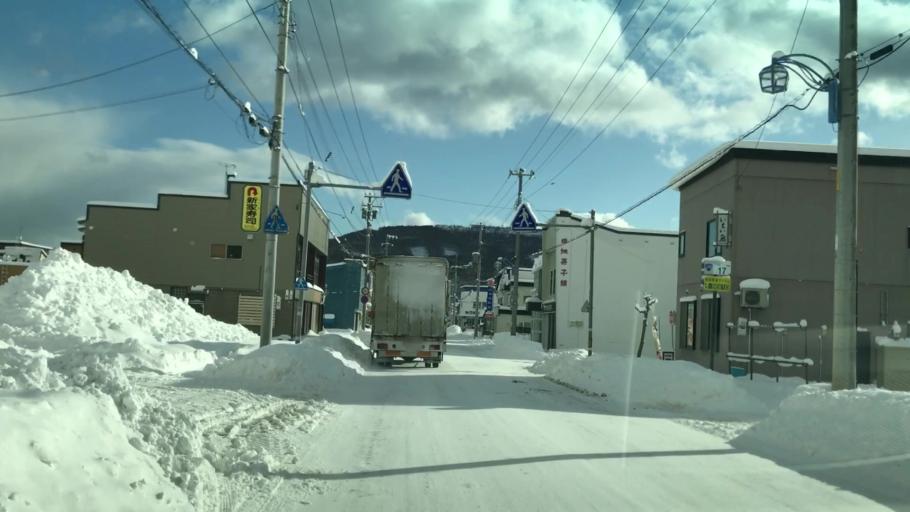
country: JP
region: Hokkaido
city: Yoichi
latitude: 43.2647
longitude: 140.6407
